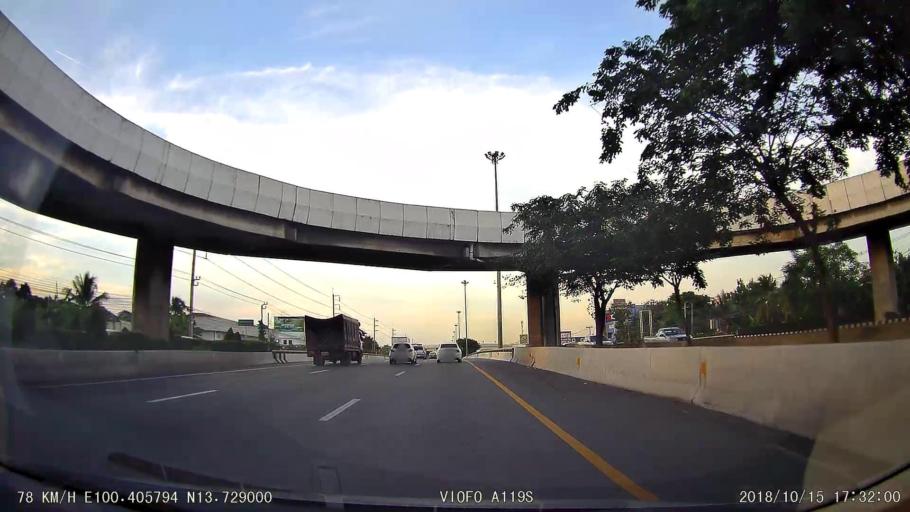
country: TH
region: Bangkok
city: Phasi Charoen
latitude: 13.7293
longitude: 100.4058
